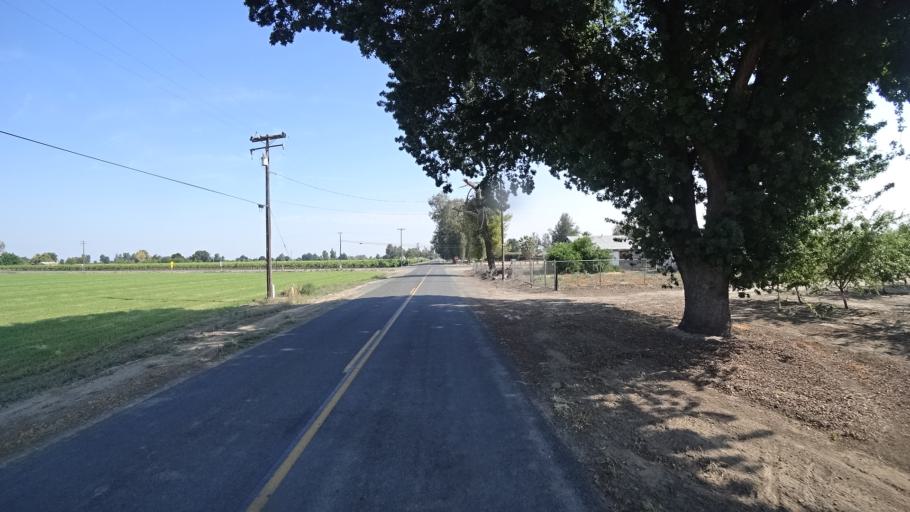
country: US
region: California
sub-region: Kings County
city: Lemoore
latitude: 36.3432
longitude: -119.8339
